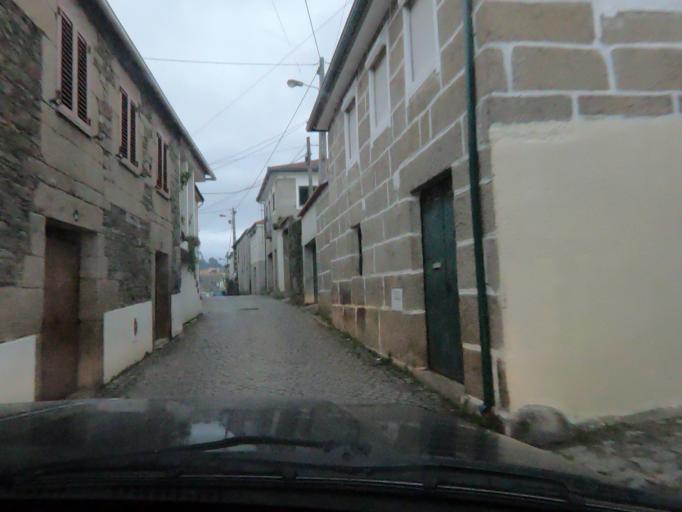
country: PT
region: Vila Real
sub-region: Vila Real
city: Vila Real
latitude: 41.2560
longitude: -7.7347
